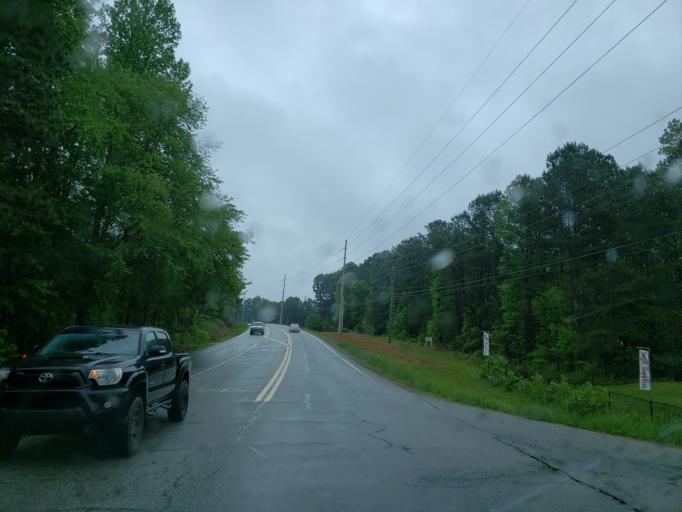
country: US
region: Georgia
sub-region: Paulding County
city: Dallas
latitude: 33.8577
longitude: -84.8456
